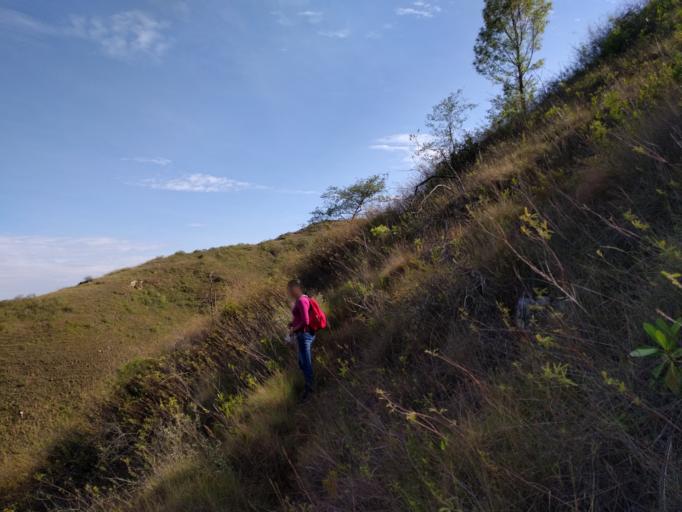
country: BO
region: Santa Cruz
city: Samaipata
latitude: -18.1838
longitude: -63.8886
